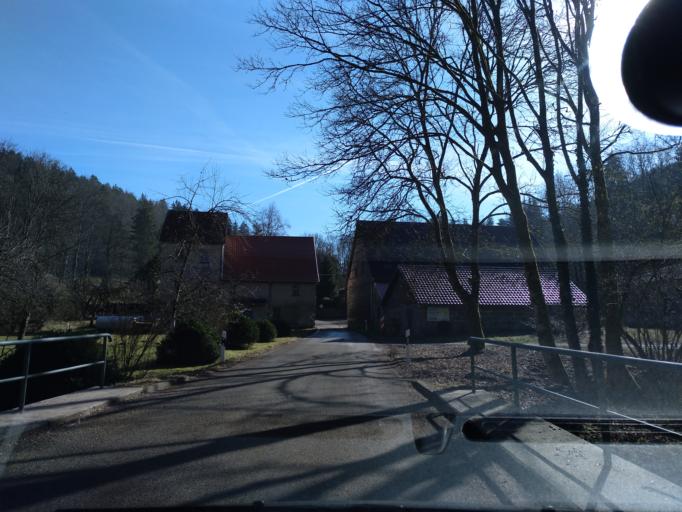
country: DE
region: Baden-Wuerttemberg
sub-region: Regierungsbezirk Stuttgart
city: Mainhardt
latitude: 49.1018
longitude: 9.5365
